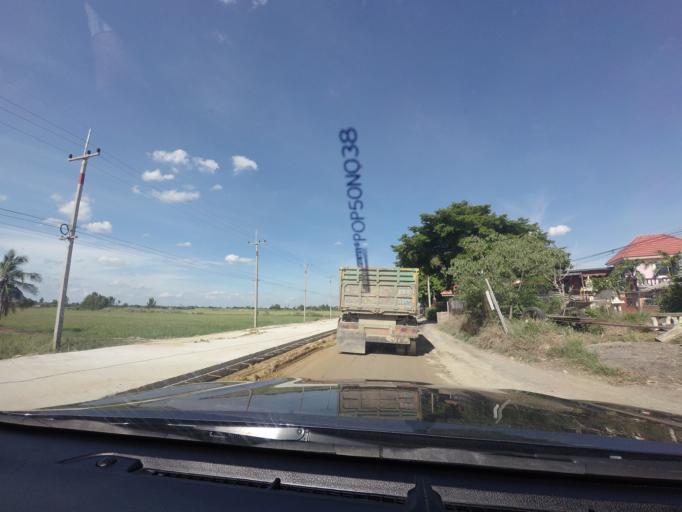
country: TH
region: Suphan Buri
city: Song Phi Nong
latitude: 14.1787
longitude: 100.0385
